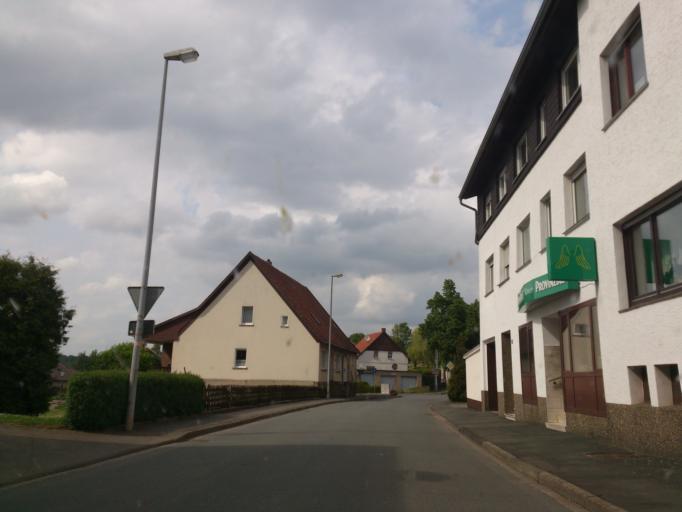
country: DE
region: North Rhine-Westphalia
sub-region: Regierungsbezirk Detmold
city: Willebadessen
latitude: 51.5596
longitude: 9.0512
